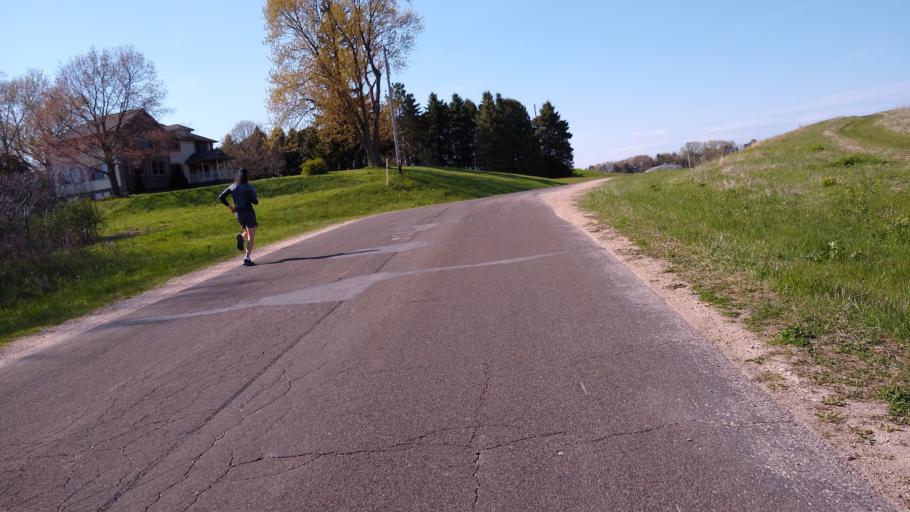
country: US
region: Wisconsin
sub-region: Dane County
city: Waunakee
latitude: 43.1417
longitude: -89.4381
